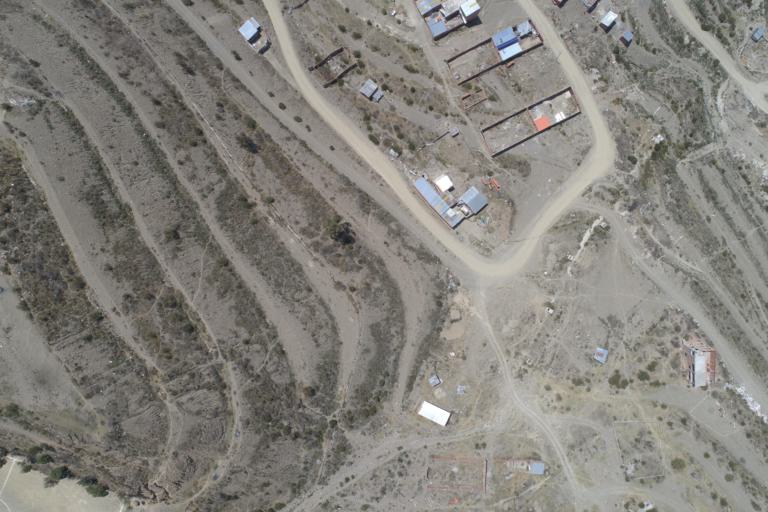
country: BO
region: La Paz
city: La Paz
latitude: -16.5012
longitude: -68.0981
